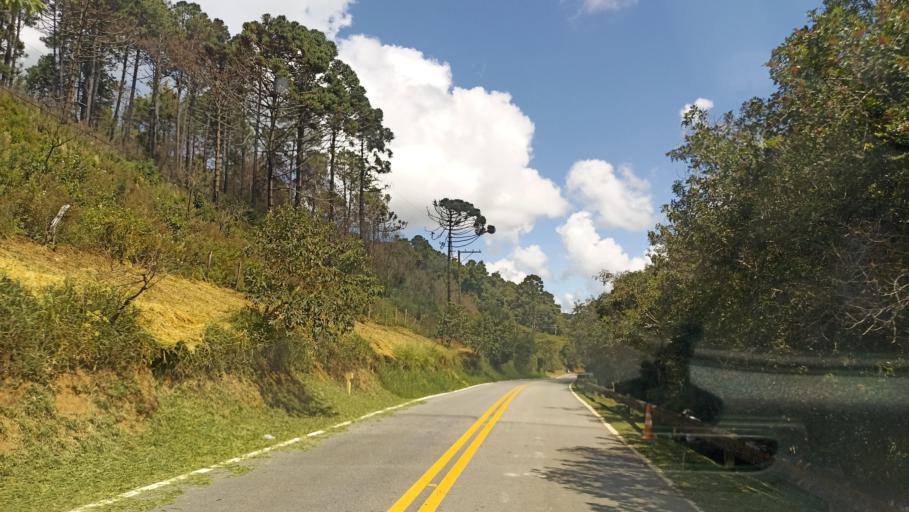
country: BR
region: Sao Paulo
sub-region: Cunha
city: Cunha
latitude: -23.1372
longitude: -44.9140
